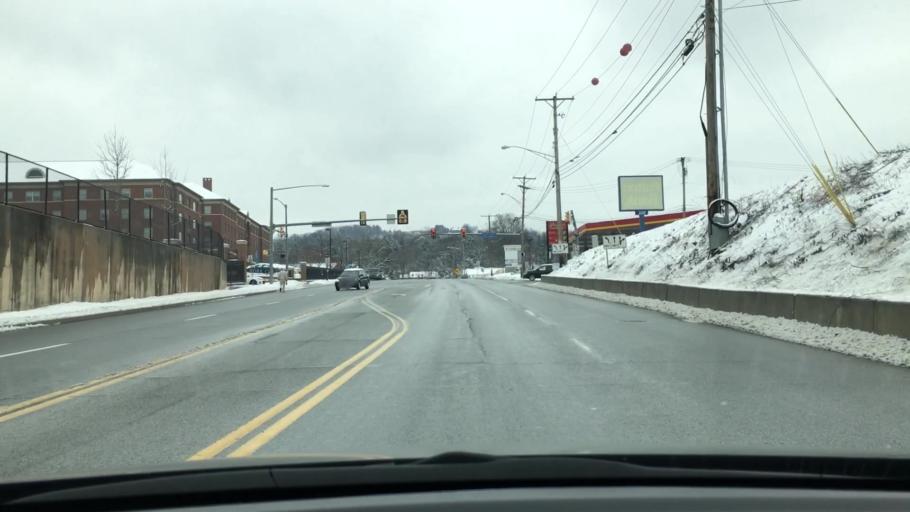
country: US
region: Pennsylvania
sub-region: York County
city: West York
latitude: 39.9446
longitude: -76.7414
